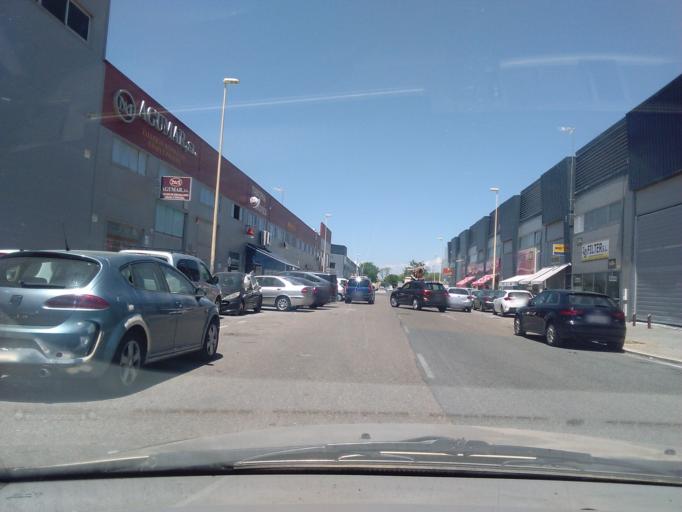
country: ES
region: Andalusia
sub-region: Provincia de Sevilla
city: Sevilla
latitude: 37.3826
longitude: -5.9302
